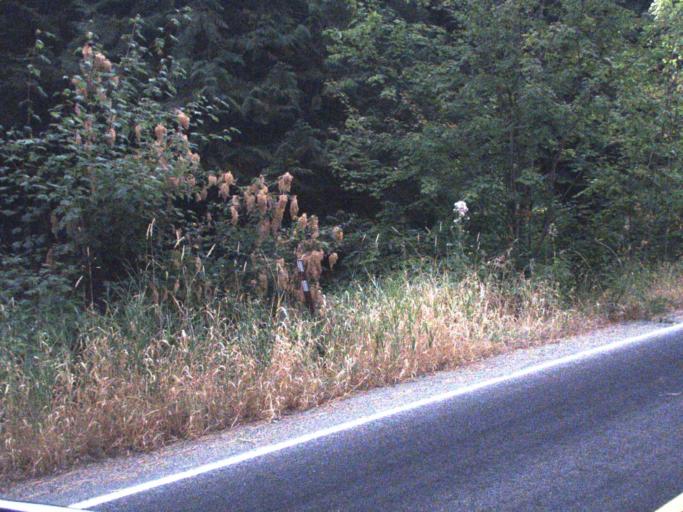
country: US
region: Washington
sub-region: Spokane County
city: Trentwood
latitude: 47.8359
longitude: -117.1827
